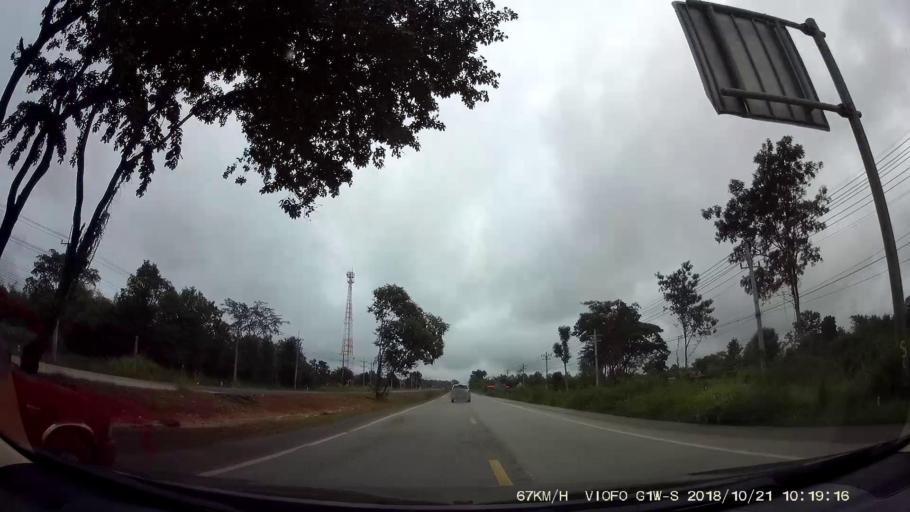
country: TH
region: Chaiyaphum
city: Phu Khiao
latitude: 16.3161
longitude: 102.1974
